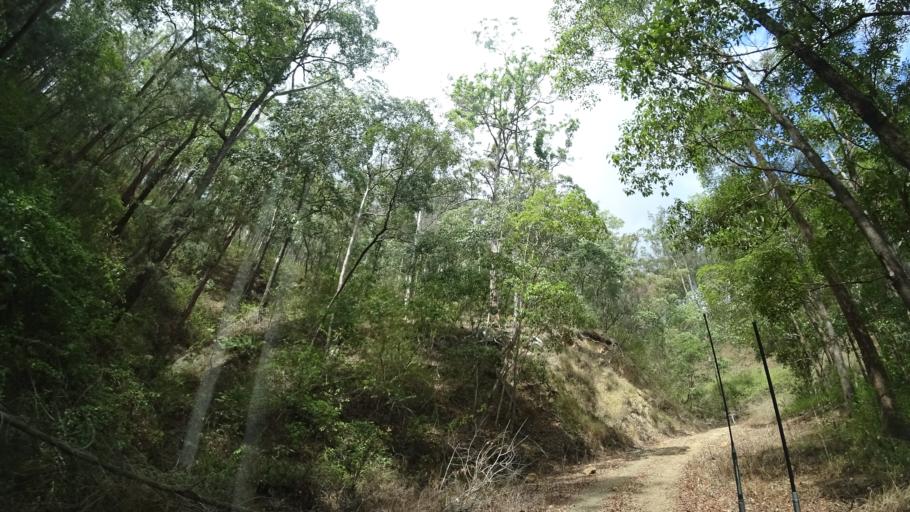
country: AU
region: Queensland
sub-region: Moreton Bay
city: Highvale
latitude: -27.3550
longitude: 152.7287
